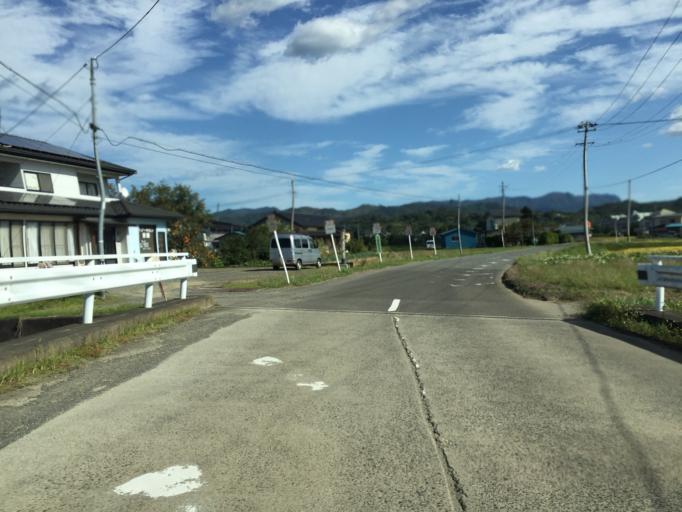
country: JP
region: Fukushima
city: Yanagawamachi-saiwaicho
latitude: 37.8405
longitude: 140.5908
